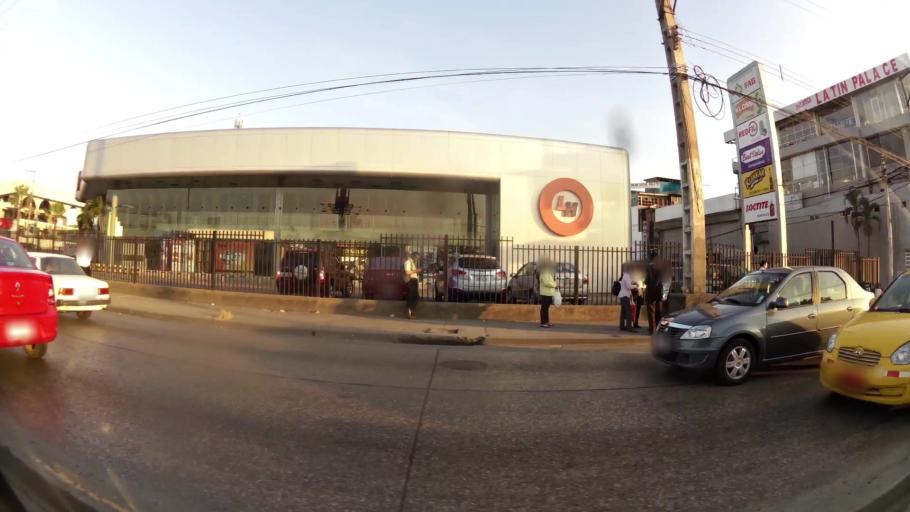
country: EC
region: Guayas
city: Guayaquil
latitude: -2.1479
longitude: -79.9065
